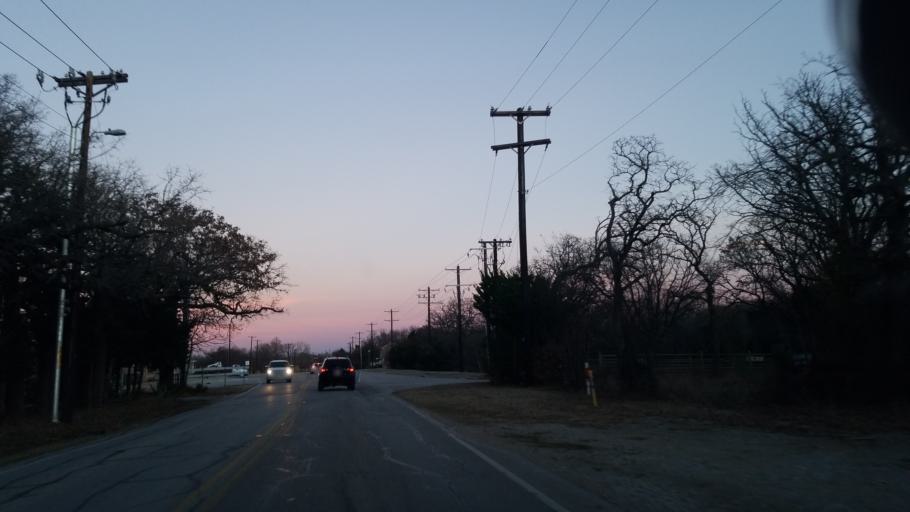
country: US
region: Texas
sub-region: Denton County
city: Corinth
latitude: 33.1615
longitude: -97.1138
